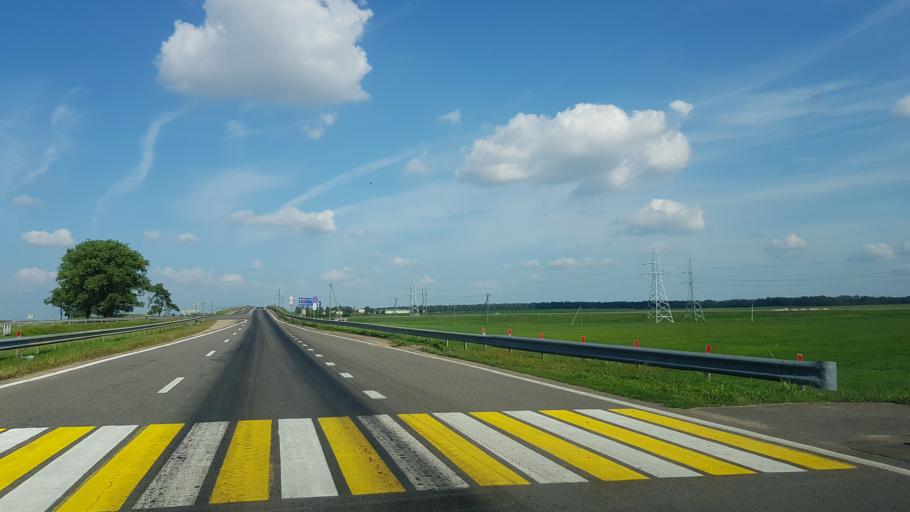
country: BY
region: Minsk
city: Dzyarzhynsk
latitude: 53.7043
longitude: 27.2097
